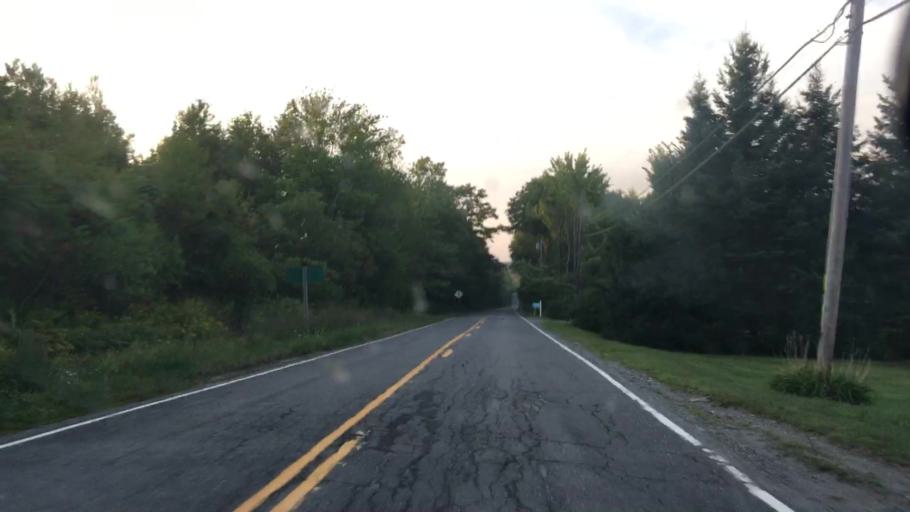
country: US
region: Maine
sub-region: Waldo County
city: Frankfort
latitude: 44.6992
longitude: -68.9449
